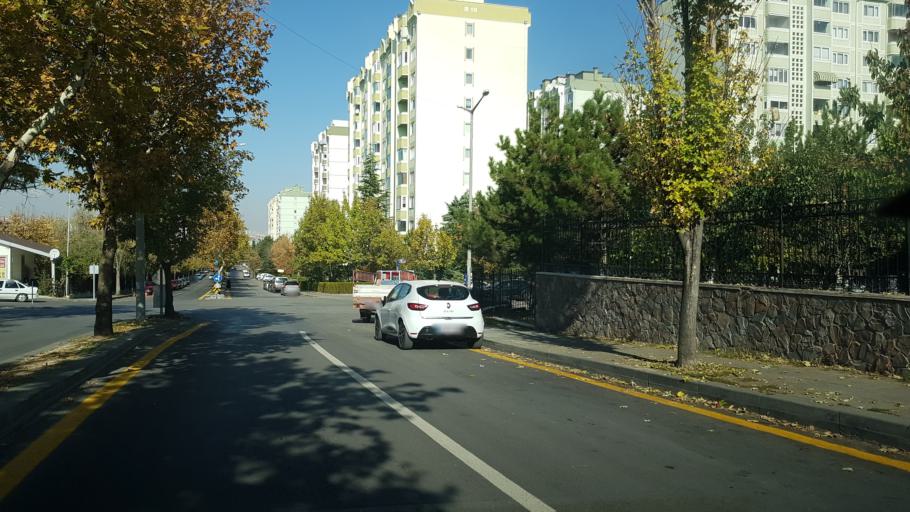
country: TR
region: Ankara
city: Etimesgut
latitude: 39.9522
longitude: 32.6050
